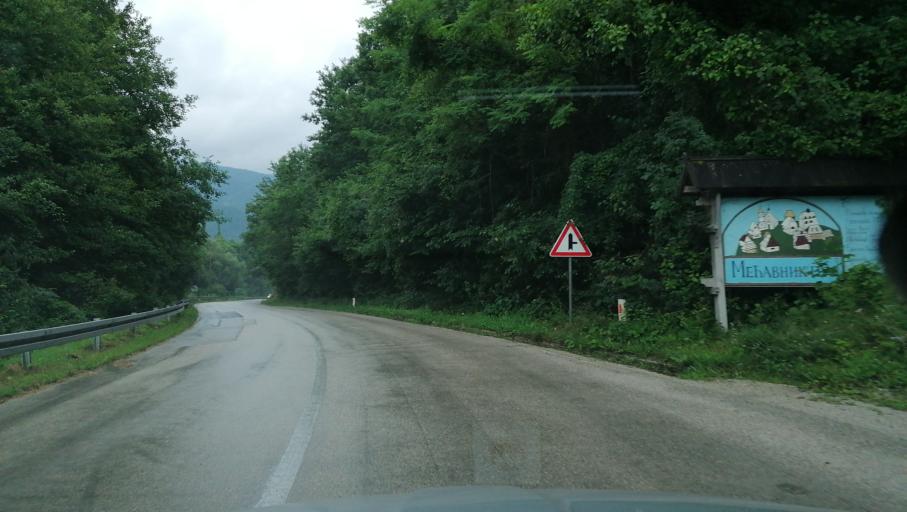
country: RS
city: Durici
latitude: 43.8015
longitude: 19.5047
